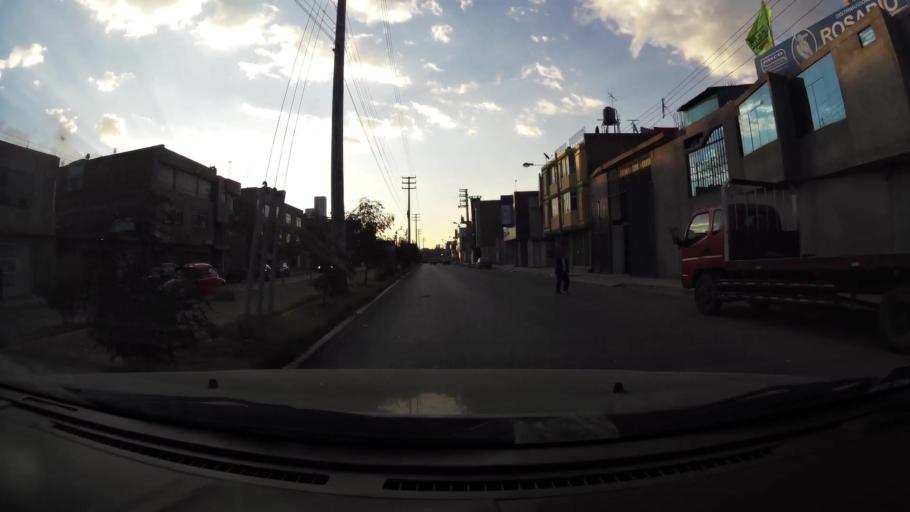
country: PE
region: Junin
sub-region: Provincia de Huancayo
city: El Tambo
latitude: -12.0499
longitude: -75.2282
